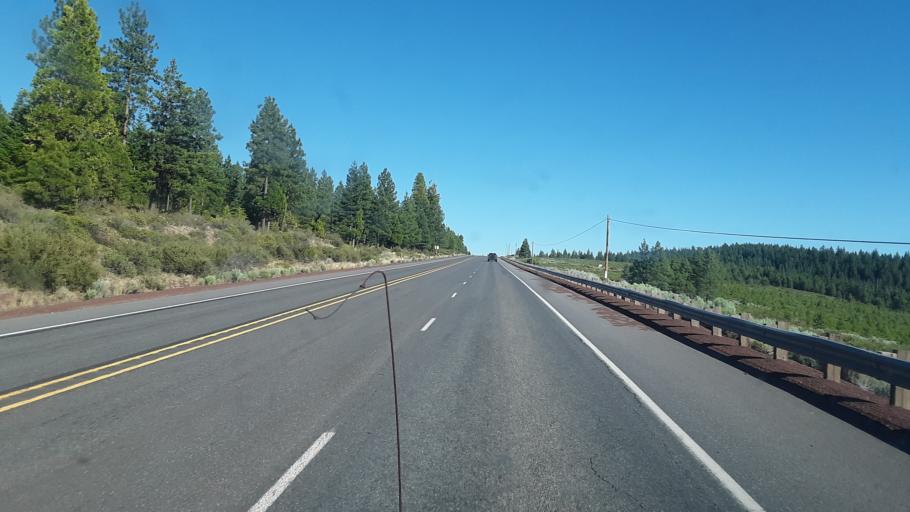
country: US
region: Oregon
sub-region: Klamath County
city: Klamath Falls
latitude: 42.3572
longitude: -121.9889
